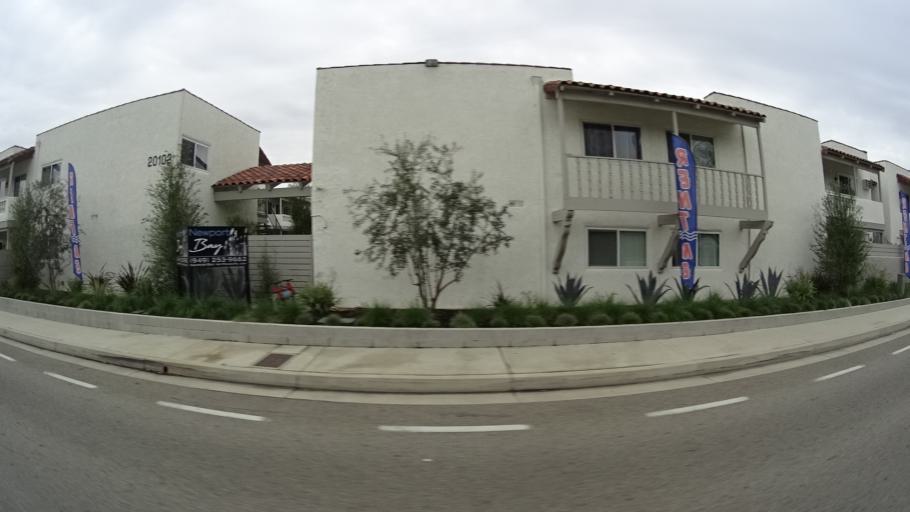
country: US
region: California
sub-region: Orange County
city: Costa Mesa
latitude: 33.6592
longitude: -117.8752
